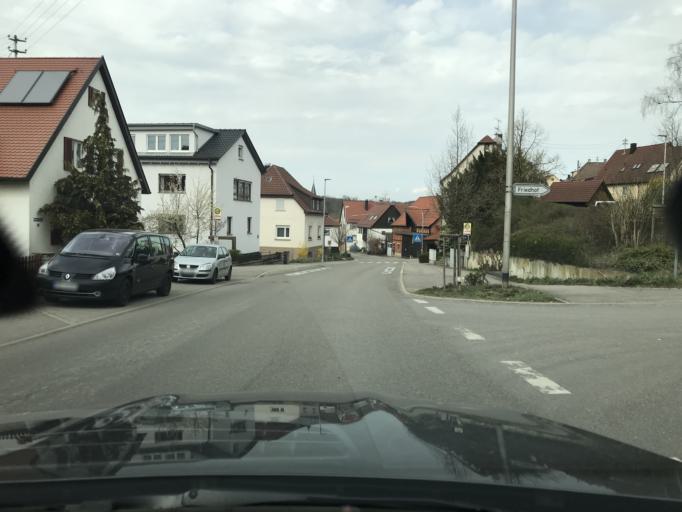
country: DE
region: Baden-Wuerttemberg
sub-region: Regierungsbezirk Stuttgart
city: Burgstetten
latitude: 48.9270
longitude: 9.3728
